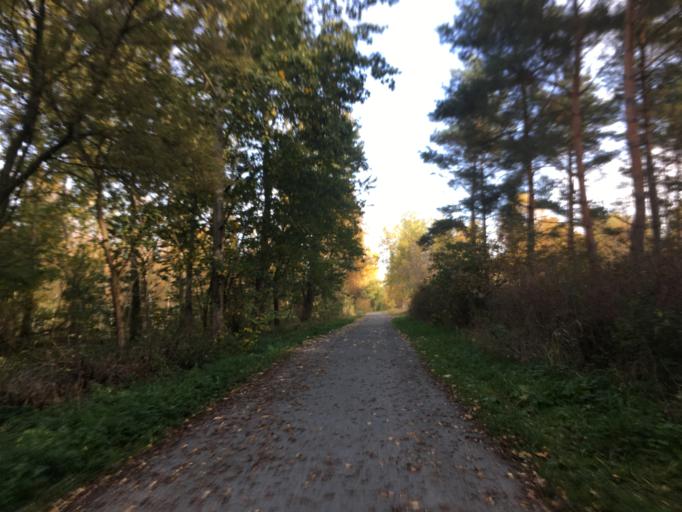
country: DE
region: Berlin
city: Buch
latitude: 52.6609
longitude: 13.4840
